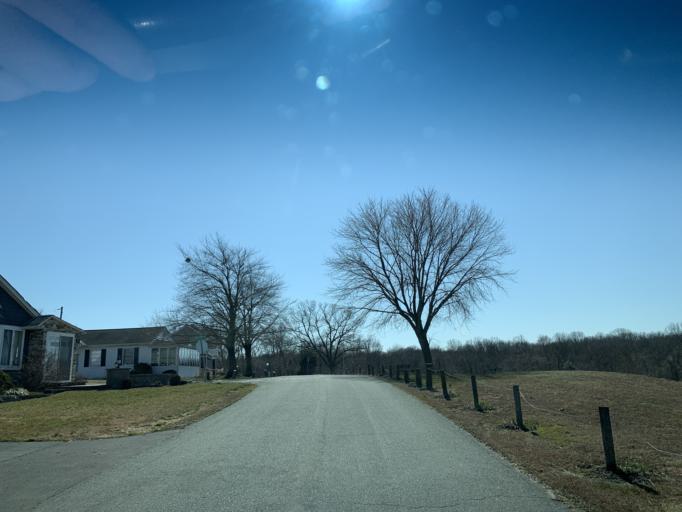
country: US
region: Maryland
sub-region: Cecil County
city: Charlestown
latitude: 39.4378
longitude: -75.9781
